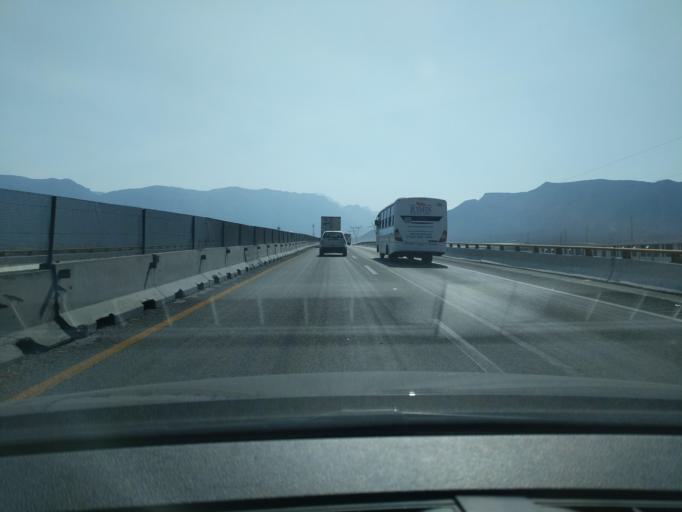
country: MX
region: Nuevo Leon
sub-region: Garcia
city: Los Parques
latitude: 25.7392
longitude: -100.5187
